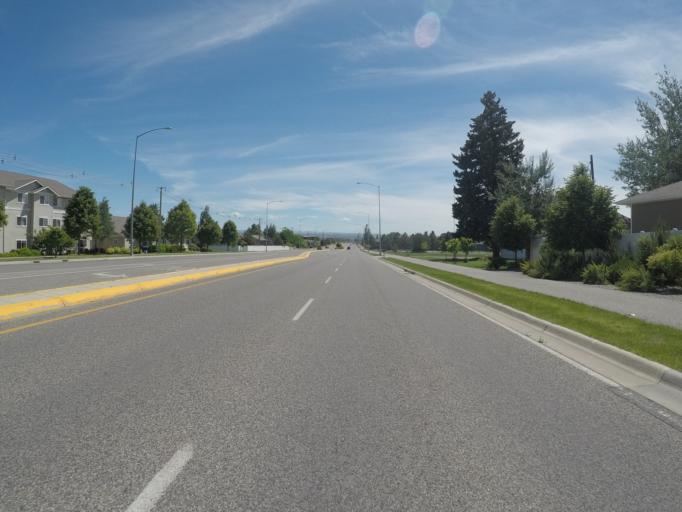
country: US
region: Montana
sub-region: Yellowstone County
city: Billings
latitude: 45.7901
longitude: -108.6177
